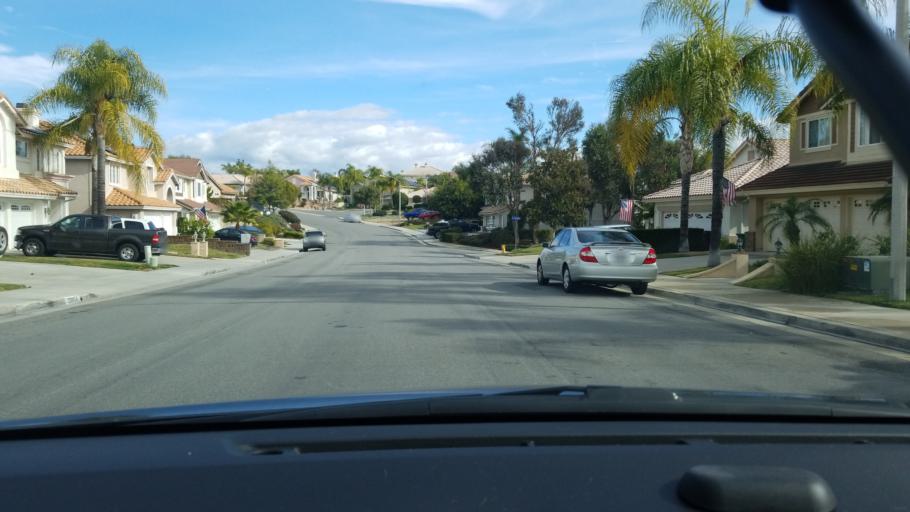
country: US
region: California
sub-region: Riverside County
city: Murrieta
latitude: 33.5963
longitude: -117.1946
